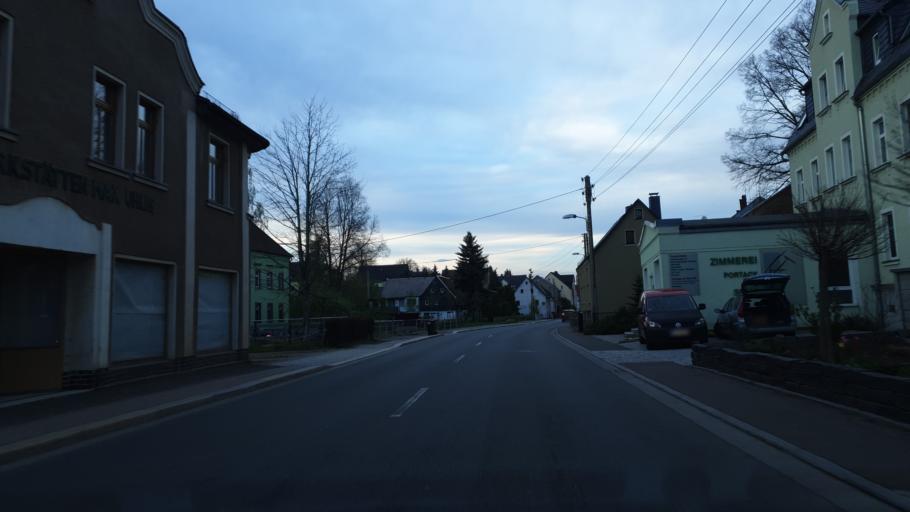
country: DE
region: Saxony
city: Gersdorf
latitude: 50.7535
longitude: 12.7077
